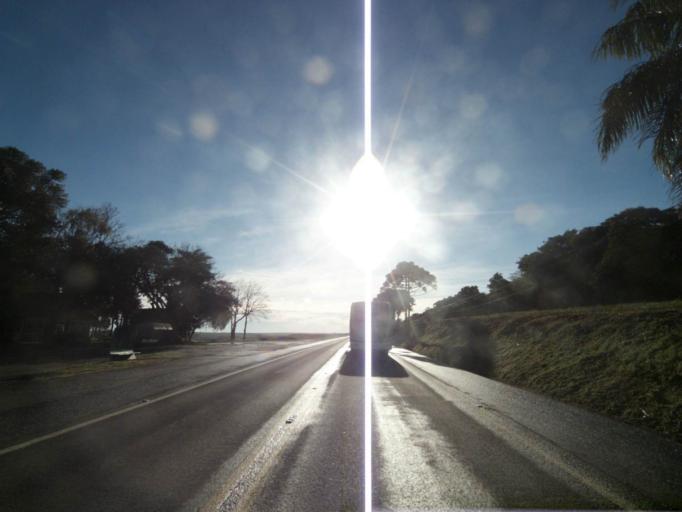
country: BR
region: Parana
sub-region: Matelandia
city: Matelandia
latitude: -25.1113
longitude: -53.7674
